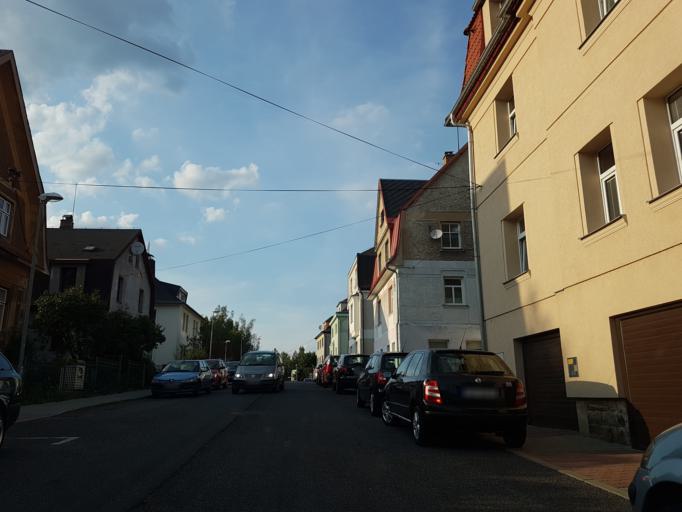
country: CZ
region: Liberecky
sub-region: Okres Jablonec nad Nisou
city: Jablonec nad Nisou
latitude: 50.7302
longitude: 15.1786
